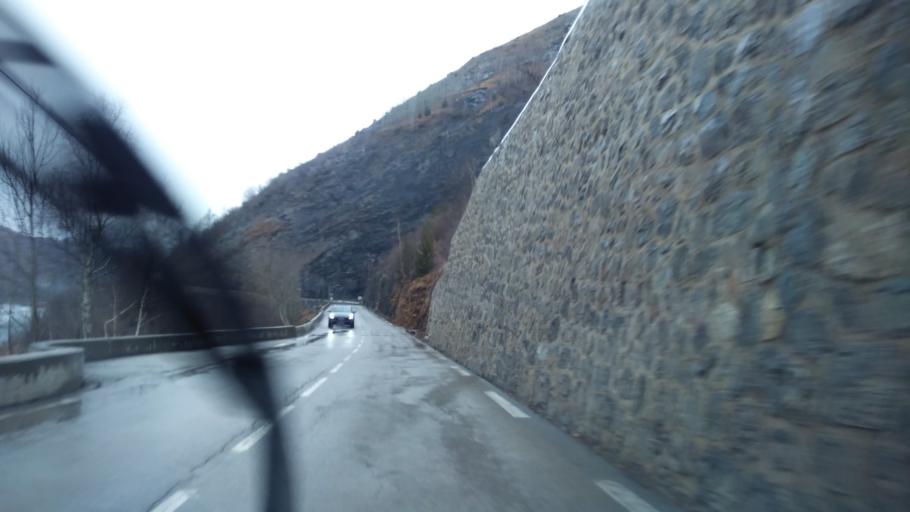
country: FR
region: Rhone-Alpes
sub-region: Departement de l'Isere
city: Mont-de-Lans
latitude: 45.0434
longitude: 6.1649
